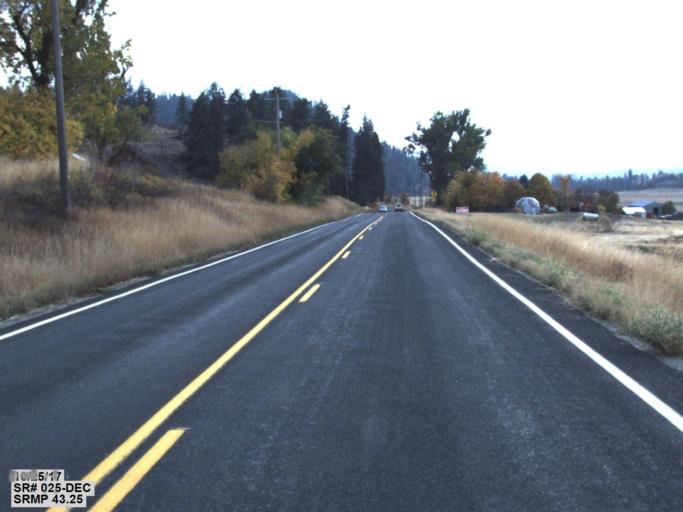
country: US
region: Washington
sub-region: Lincoln County
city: Davenport
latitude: 48.1283
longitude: -118.2071
